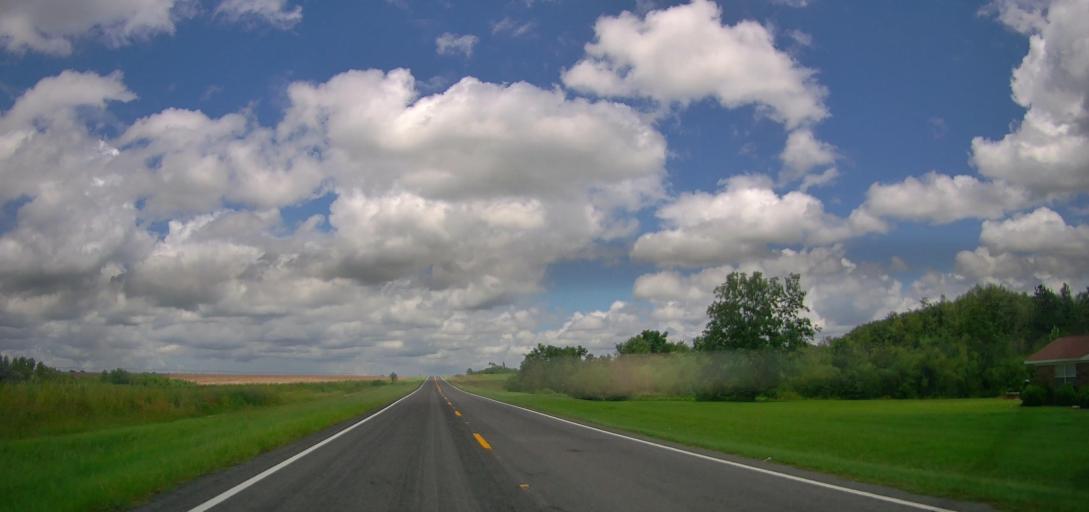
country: US
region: Georgia
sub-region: Turner County
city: Ashburn
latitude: 31.8138
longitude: -83.5697
